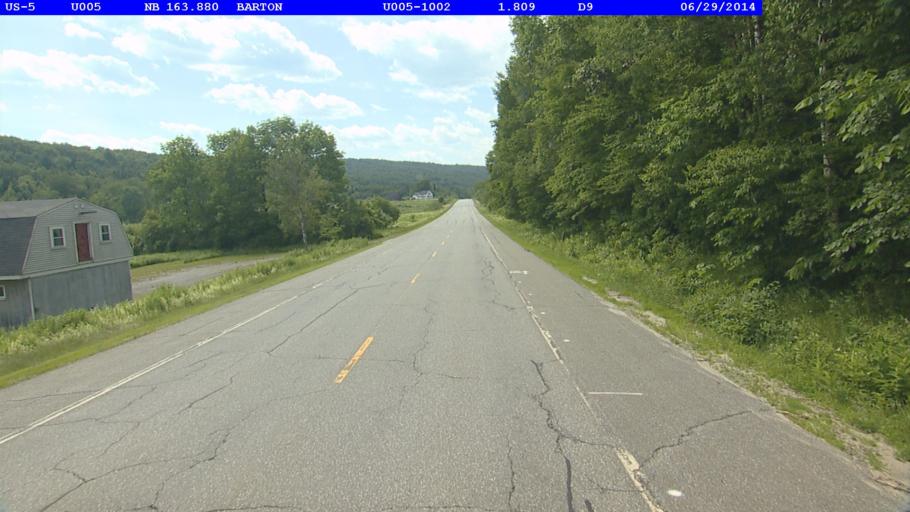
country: US
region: Vermont
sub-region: Caledonia County
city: Lyndonville
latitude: 44.7128
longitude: -72.1264
